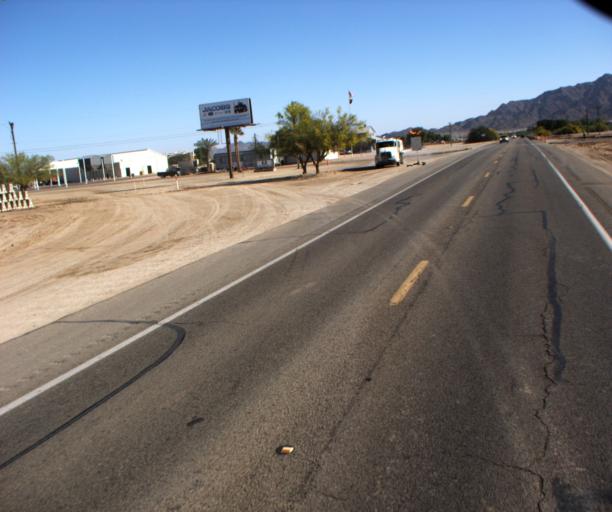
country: US
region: Arizona
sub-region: Yuma County
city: Fortuna Foothills
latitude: 32.7061
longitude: -114.4346
